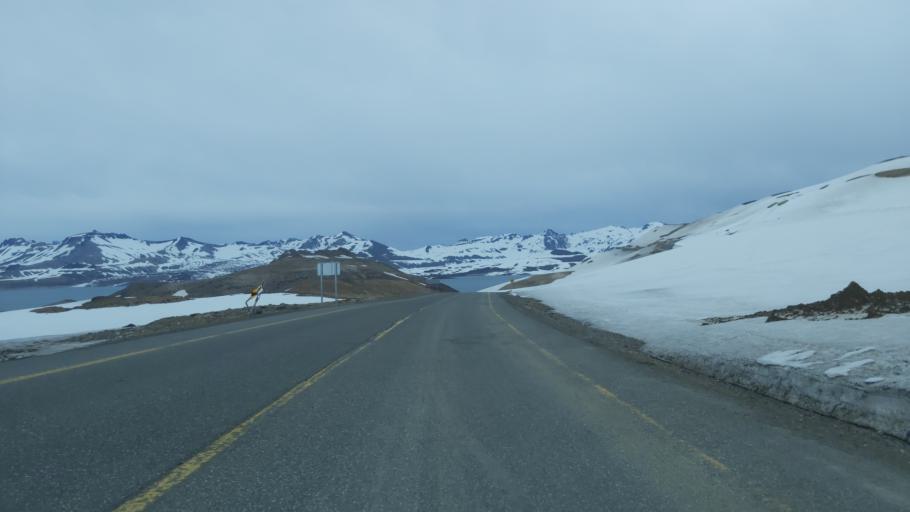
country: CL
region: Maule
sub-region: Provincia de Linares
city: Colbun
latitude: -36.0111
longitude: -70.4832
